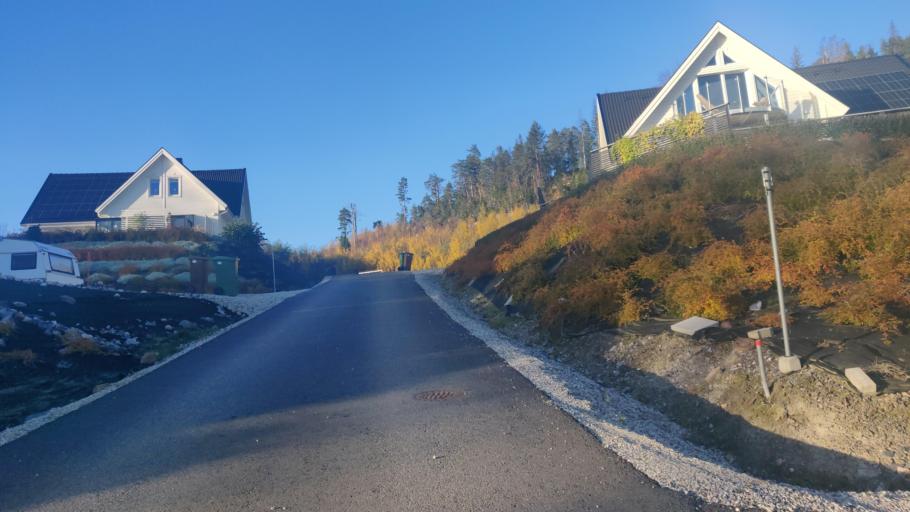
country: SE
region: Vaesternorrland
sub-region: Sundsvalls Kommun
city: Skottsund
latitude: 62.2906
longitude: 17.3945
